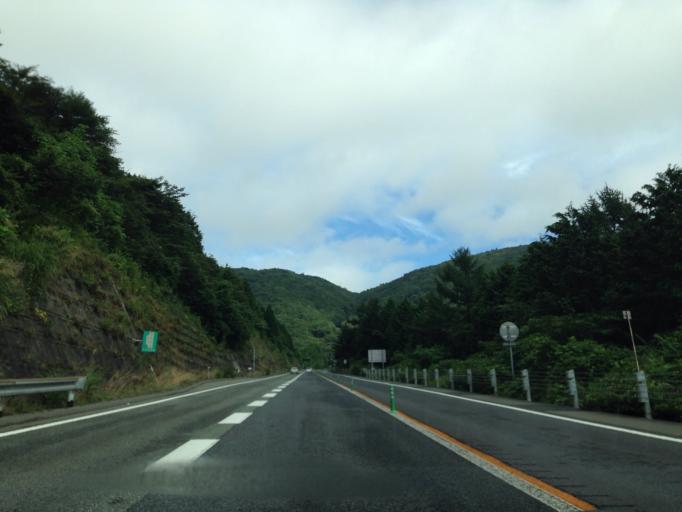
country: JP
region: Shizuoka
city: Gotemba
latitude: 35.3750
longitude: 138.8477
